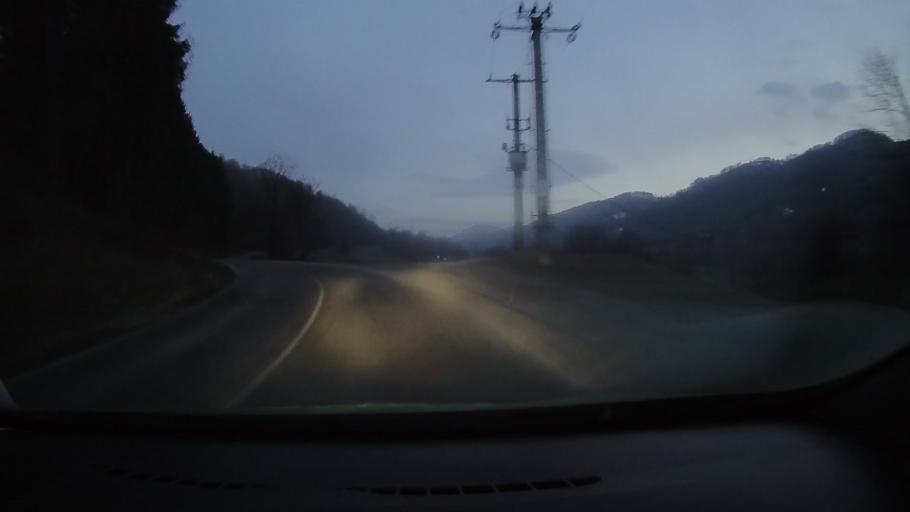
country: RO
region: Prahova
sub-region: Comuna Valea Doftanei
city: Tesila
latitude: 45.2747
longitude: 25.7316
